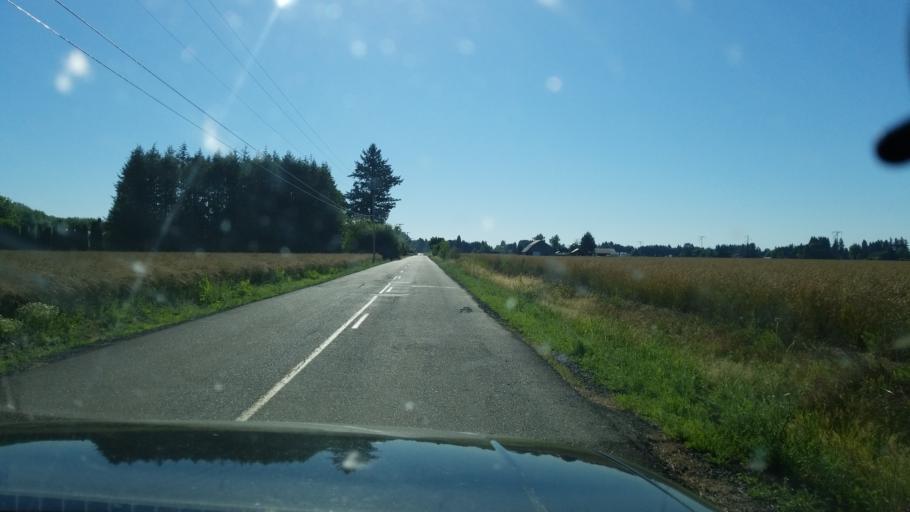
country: US
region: Oregon
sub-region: Yamhill County
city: McMinnville
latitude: 45.2449
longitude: -123.2121
